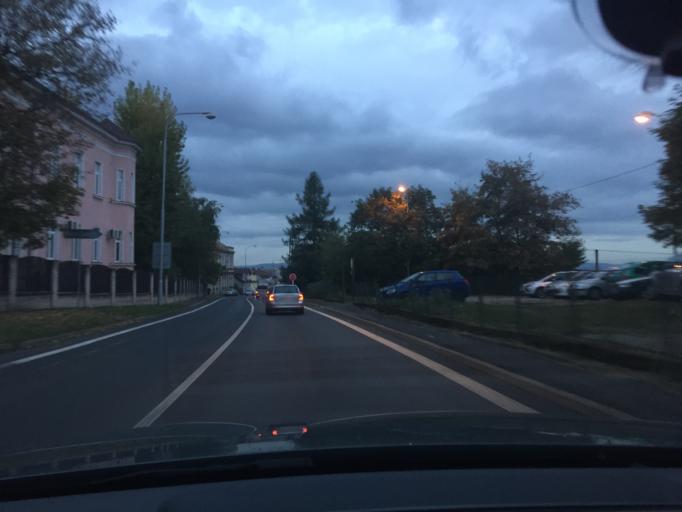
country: CZ
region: Ustecky
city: Dubi
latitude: 50.6659
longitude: 13.7950
